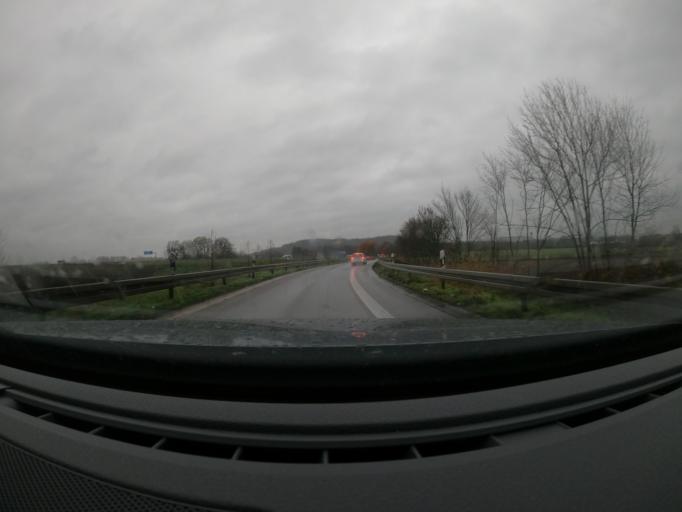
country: DE
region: North Rhine-Westphalia
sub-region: Regierungsbezirk Dusseldorf
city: Kamp-Lintfort
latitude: 51.4872
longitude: 6.5781
